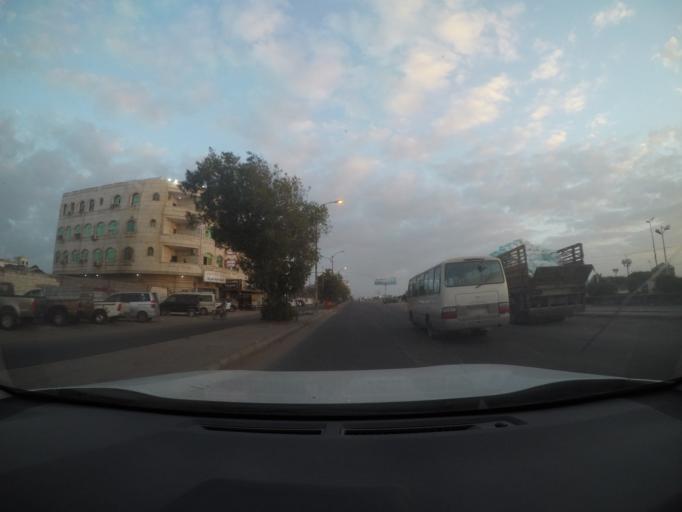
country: YE
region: Aden
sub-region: Khur Maksar
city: Khawr Maksar
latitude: 12.8419
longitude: 45.0518
